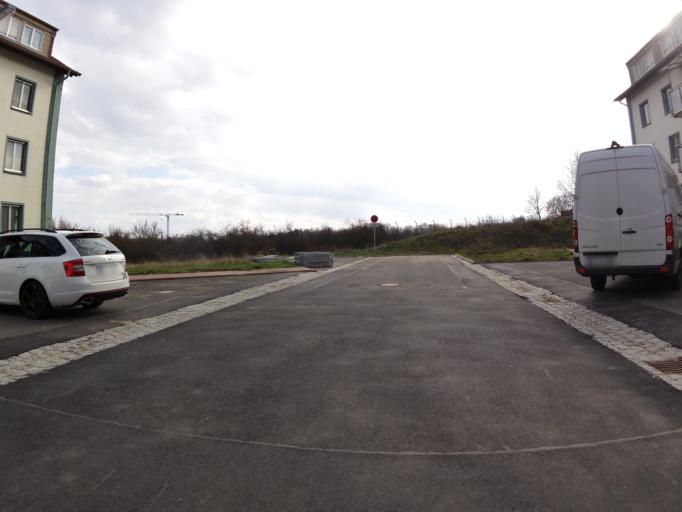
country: DE
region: Bavaria
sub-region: Regierungsbezirk Unterfranken
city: Kitzingen
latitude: 49.7384
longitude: 10.1347
